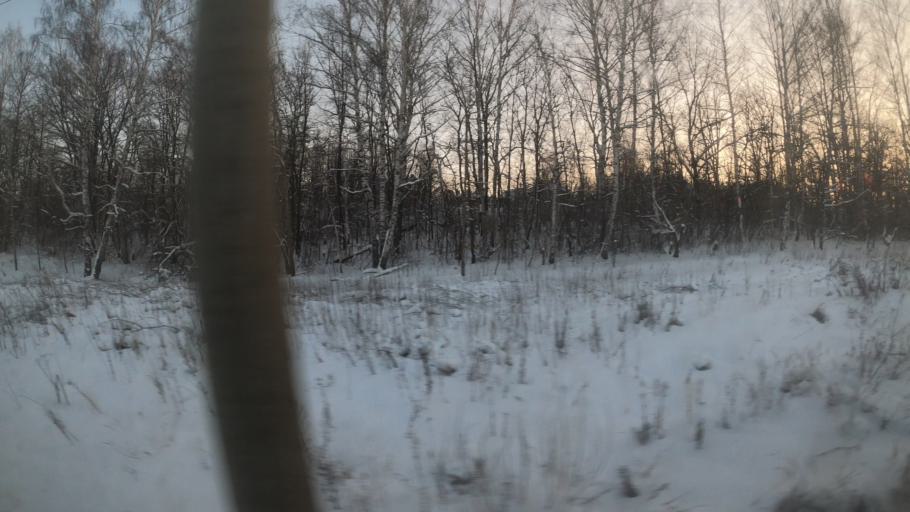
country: RU
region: Moskovskaya
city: Dedenevo
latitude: 56.2702
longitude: 37.5084
